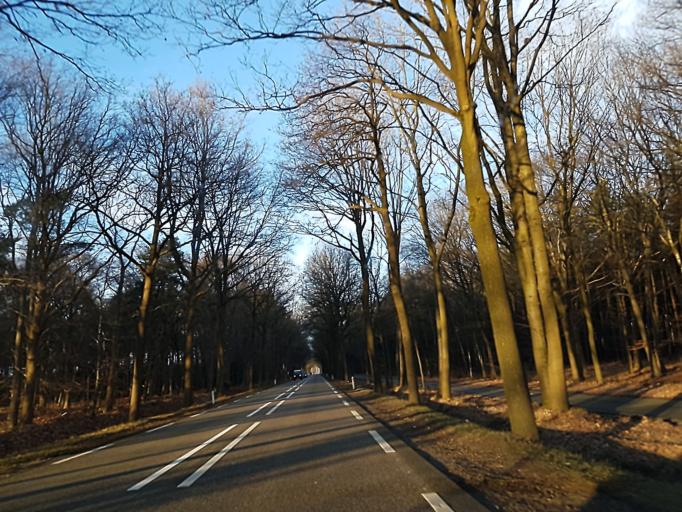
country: NL
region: North Brabant
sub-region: Gemeente Goirle
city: Goirle
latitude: 51.4807
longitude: 5.0501
